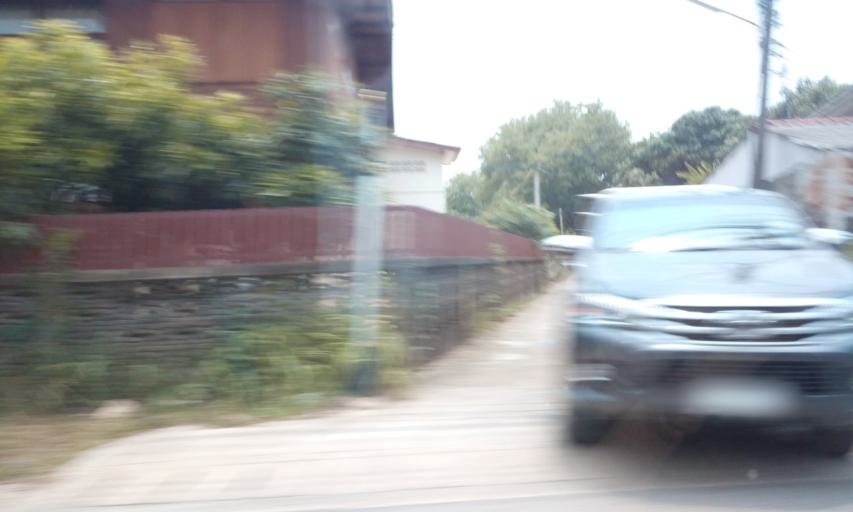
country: TH
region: Phayao
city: Chiang Kham
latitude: 19.5225
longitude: 100.3064
